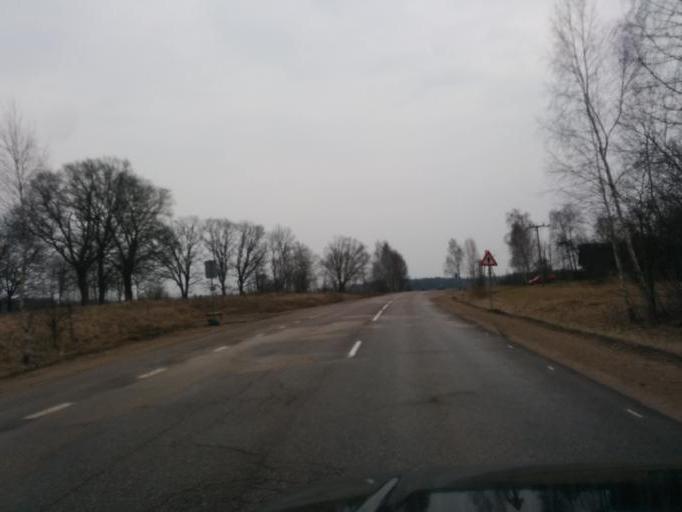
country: LV
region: Ikskile
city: Ikskile
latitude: 56.8206
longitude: 24.4459
